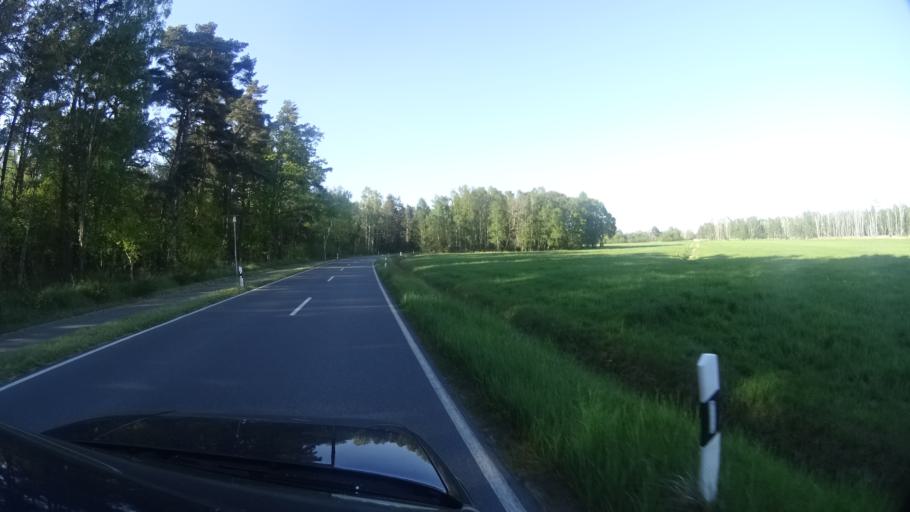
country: DE
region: Mecklenburg-Vorpommern
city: Ostseebad Dierhagen
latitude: 54.2835
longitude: 12.3232
